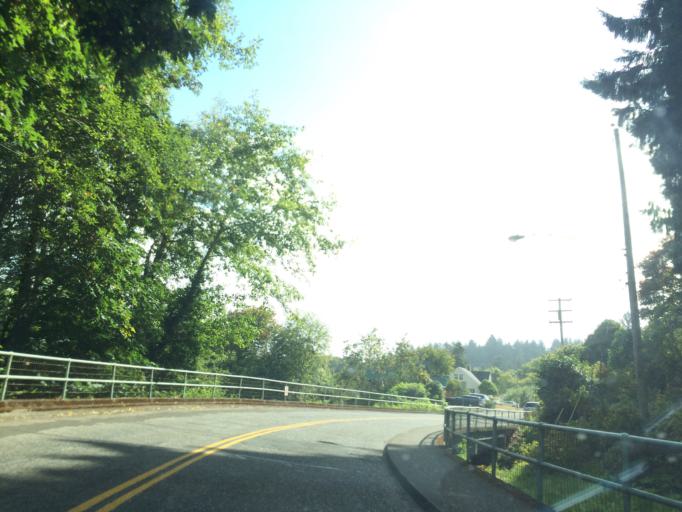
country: US
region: Oregon
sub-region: Clatsop County
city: Astoria
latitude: 46.1882
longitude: -123.8079
